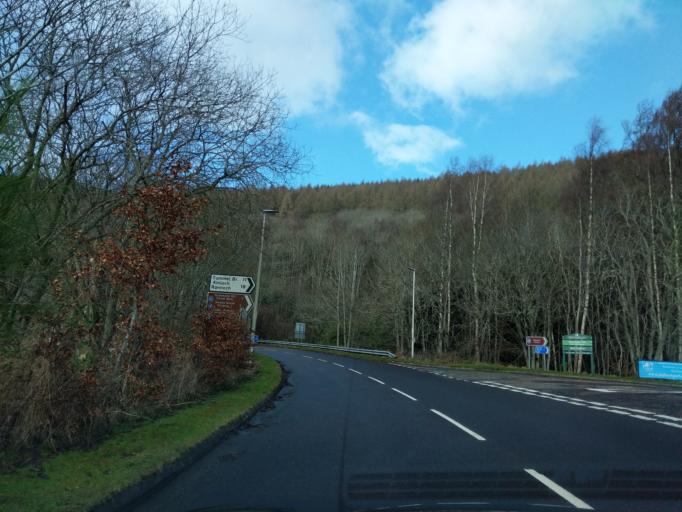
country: GB
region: Scotland
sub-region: Perth and Kinross
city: Aberfeldy
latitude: 56.5876
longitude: -4.0032
